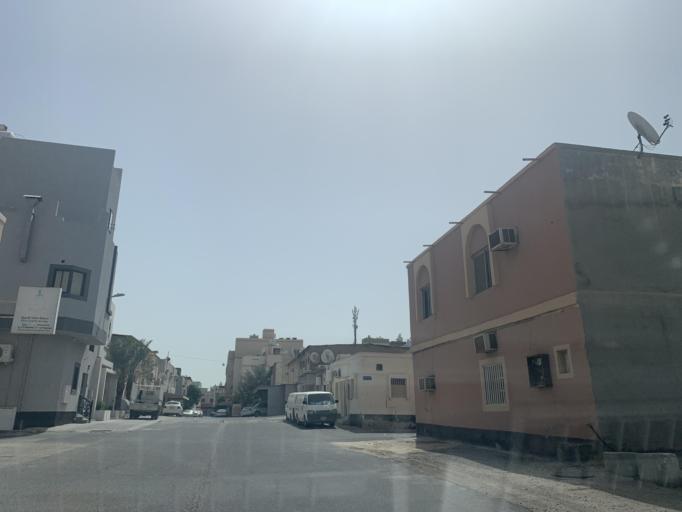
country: BH
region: Northern
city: Sitrah
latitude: 26.1636
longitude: 50.6124
